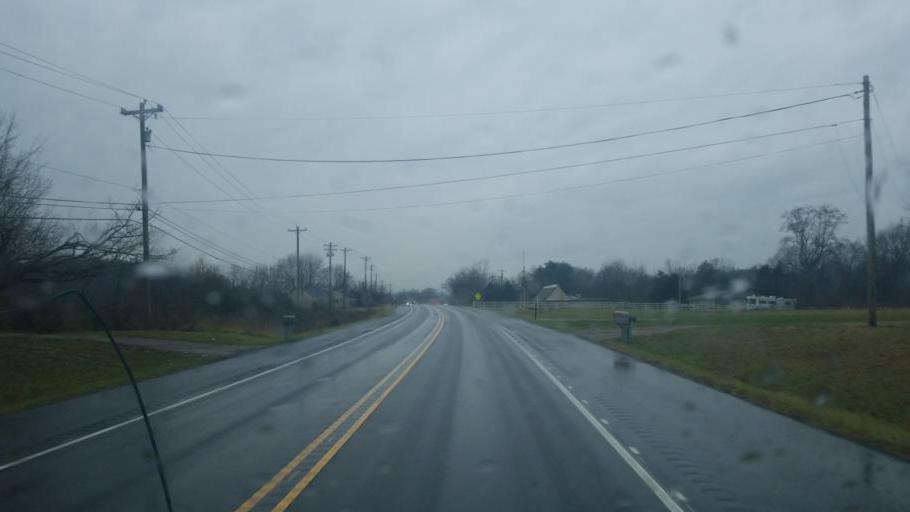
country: US
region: Indiana
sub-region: Bartholomew County
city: Columbus
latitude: 39.1989
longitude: -85.9857
